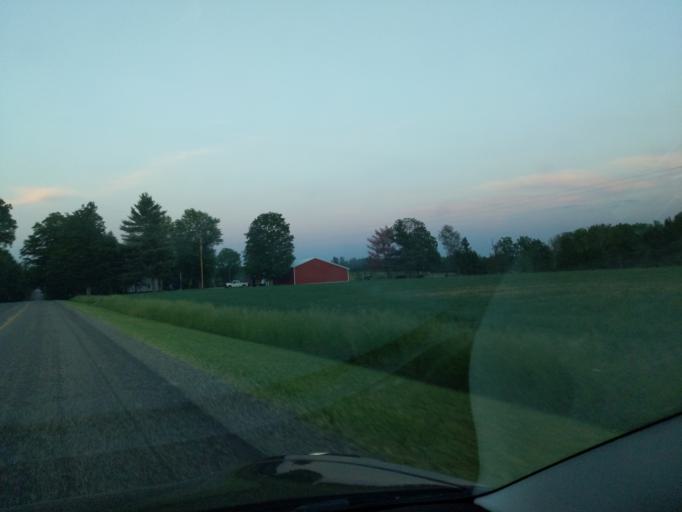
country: US
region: Michigan
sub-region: Barry County
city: Nashville
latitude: 42.5383
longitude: -85.0266
